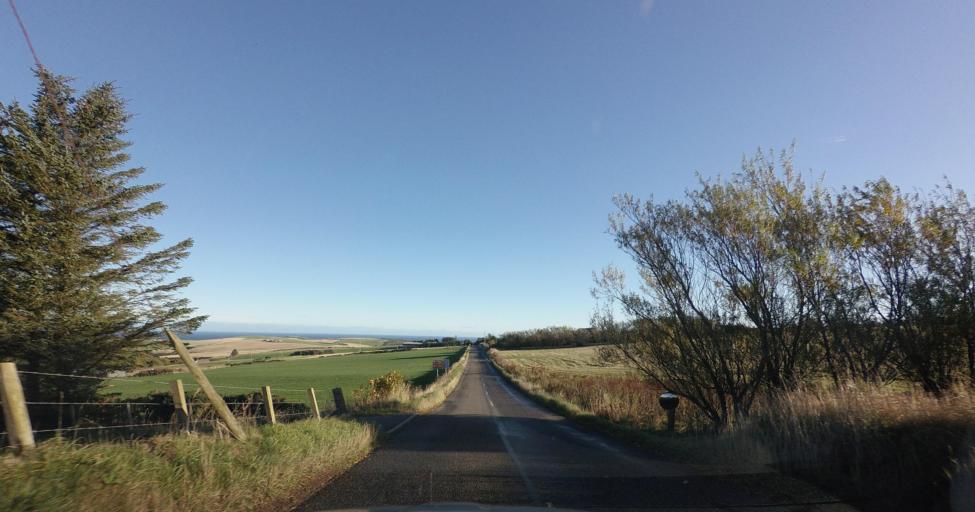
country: GB
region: Scotland
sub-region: Aberdeenshire
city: Macduff
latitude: 57.6610
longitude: -2.3225
